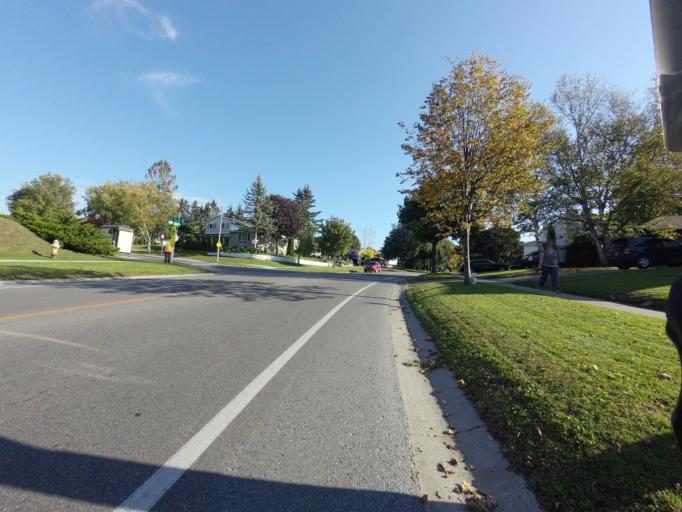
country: CA
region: Ontario
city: Kingston
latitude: 44.2345
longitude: -76.5334
